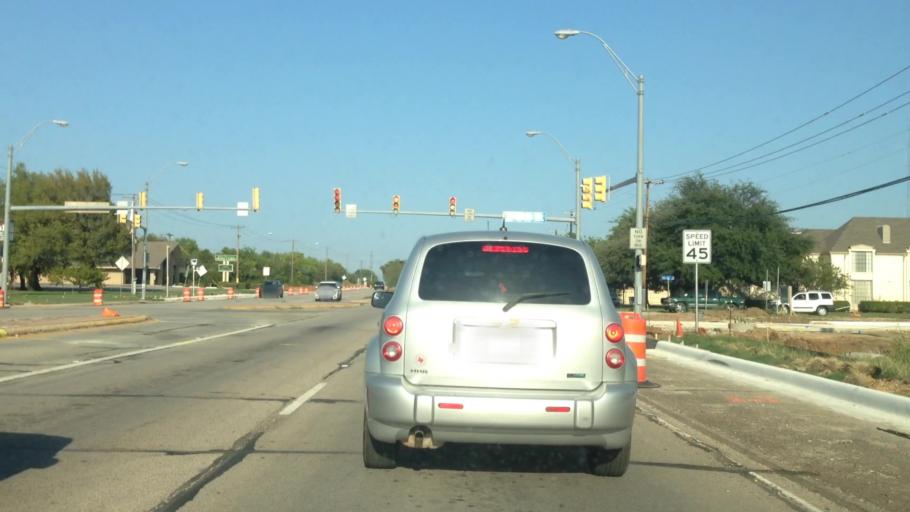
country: US
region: Texas
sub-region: Tarrant County
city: Richland Hills
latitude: 32.8091
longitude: -97.2288
